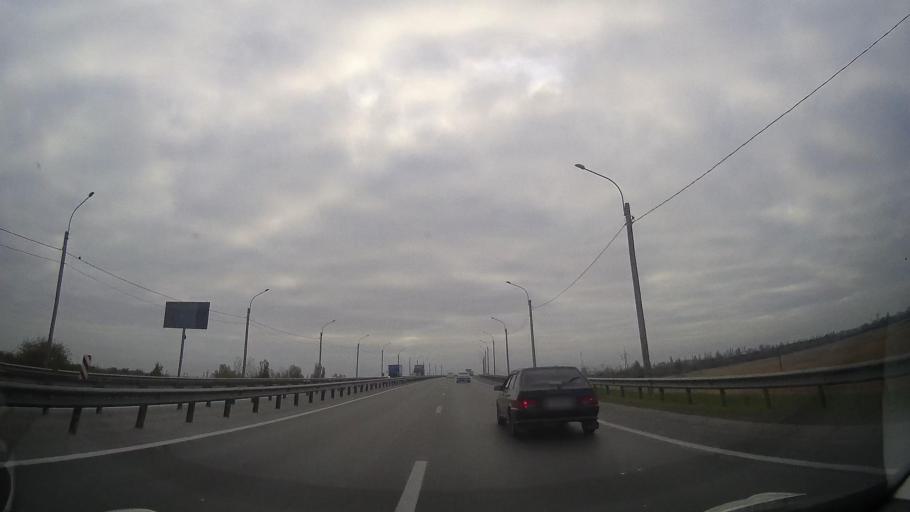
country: RU
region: Rostov
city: Bataysk
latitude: 47.1668
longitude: 39.7537
